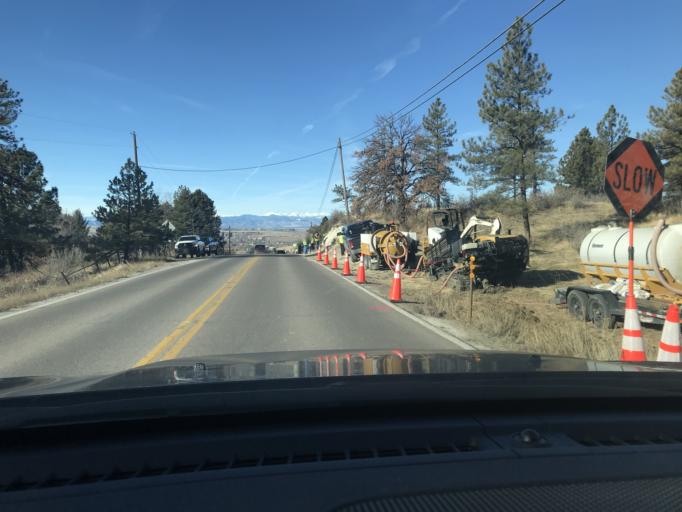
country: US
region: Colorado
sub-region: Douglas County
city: Parker
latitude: 39.5514
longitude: -104.7502
